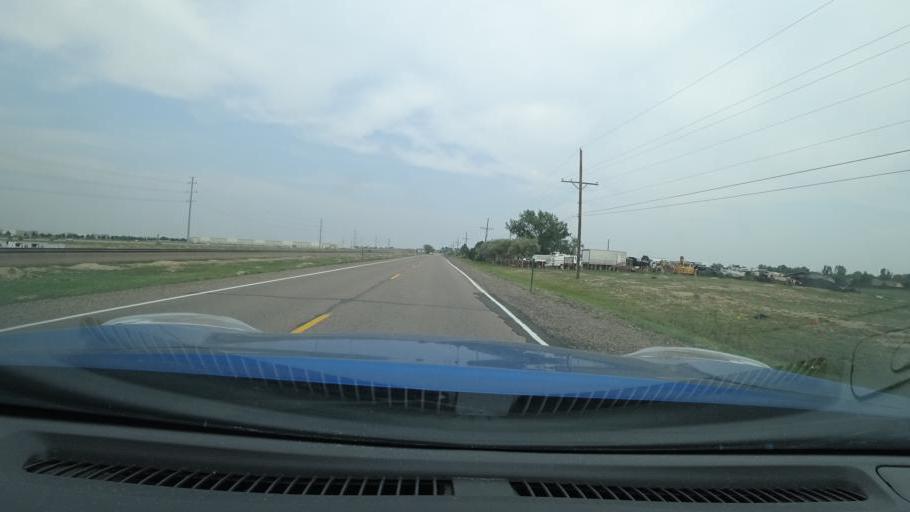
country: US
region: Colorado
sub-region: Adams County
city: Aurora
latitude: 39.7534
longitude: -104.7678
